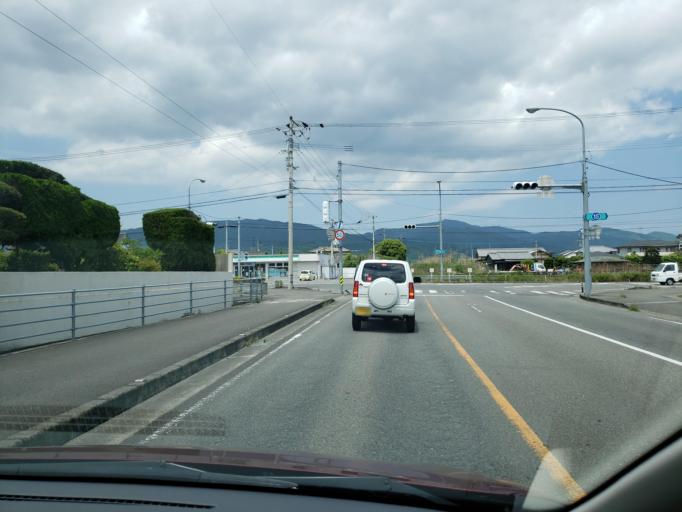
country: JP
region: Tokushima
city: Kamojimacho-jogejima
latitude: 34.0992
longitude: 134.3799
